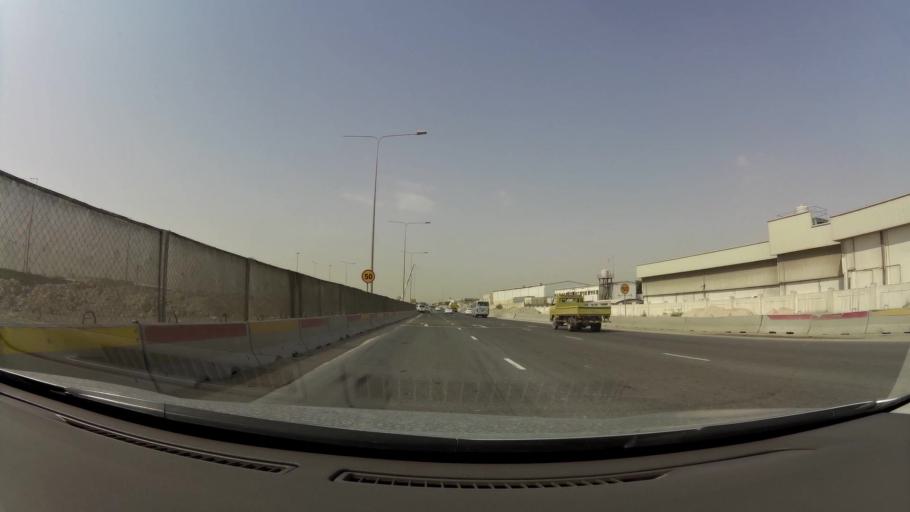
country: QA
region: Al Wakrah
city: Al Wukayr
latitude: 25.1918
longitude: 51.4514
